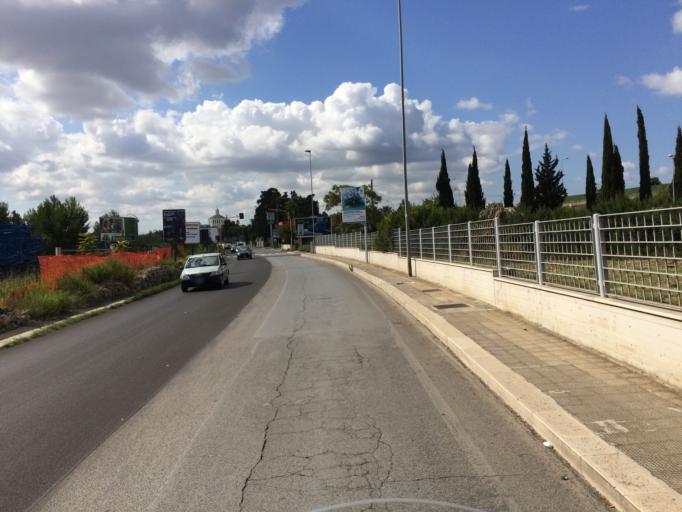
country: IT
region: Apulia
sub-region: Provincia di Bari
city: Bari
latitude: 41.1065
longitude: 16.8510
